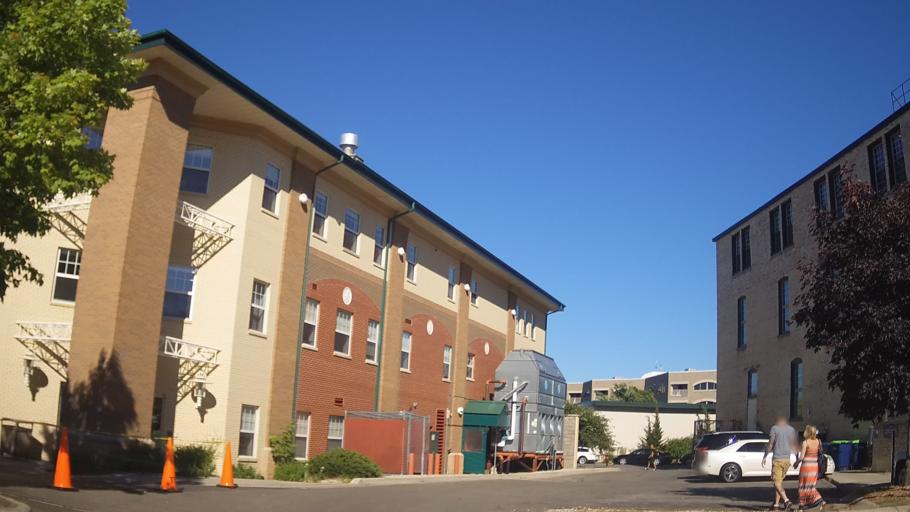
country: US
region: Michigan
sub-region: Grand Traverse County
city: Traverse City
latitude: 44.7647
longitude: -85.6288
